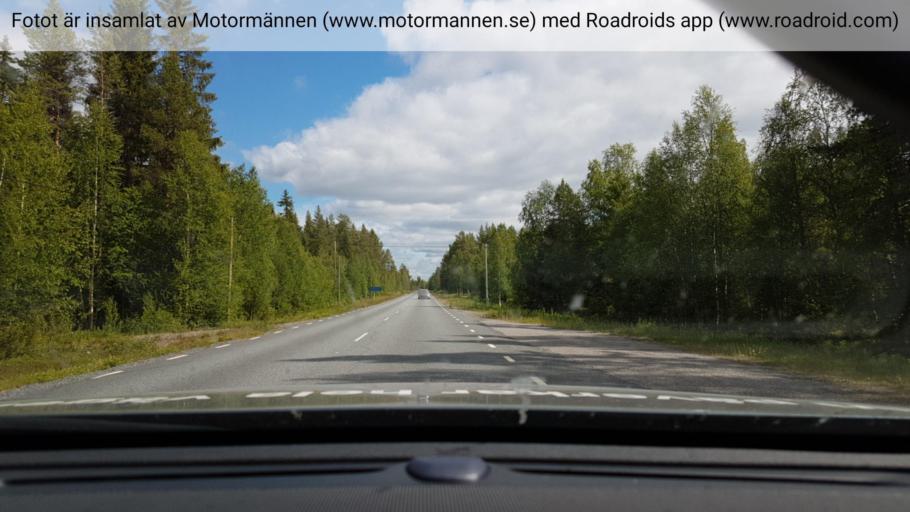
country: SE
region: Vaesterbotten
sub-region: Sorsele Kommun
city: Sorsele
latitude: 65.6669
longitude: 17.3950
